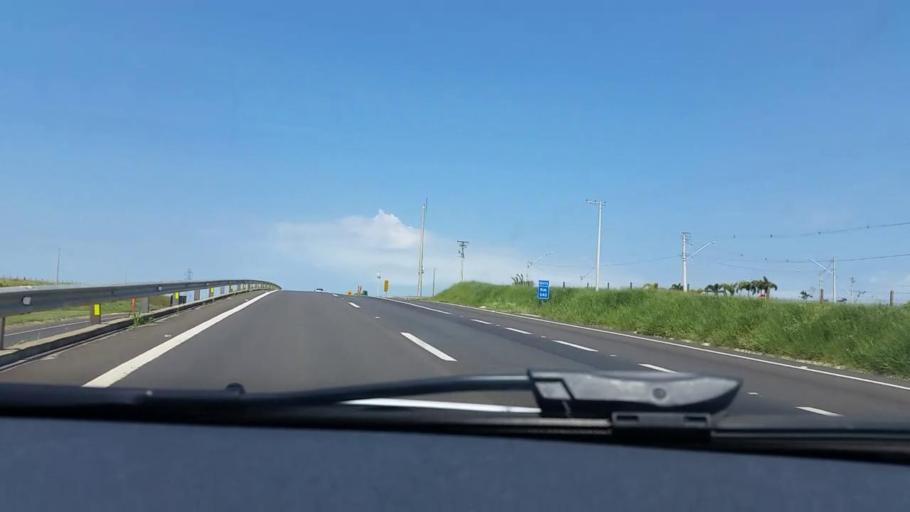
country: BR
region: Sao Paulo
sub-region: Bauru
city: Bauru
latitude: -22.3904
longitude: -49.0776
